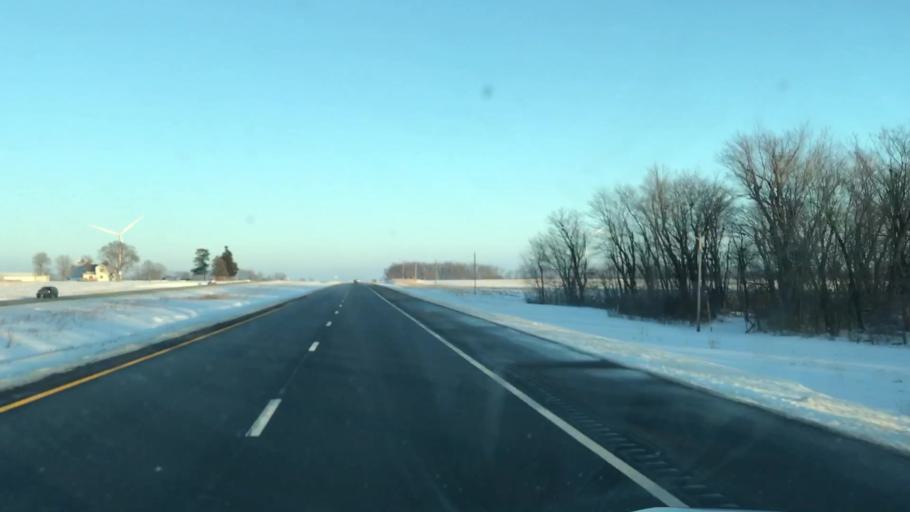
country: US
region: Missouri
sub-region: DeKalb County
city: Maysville
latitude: 39.7614
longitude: -94.3931
